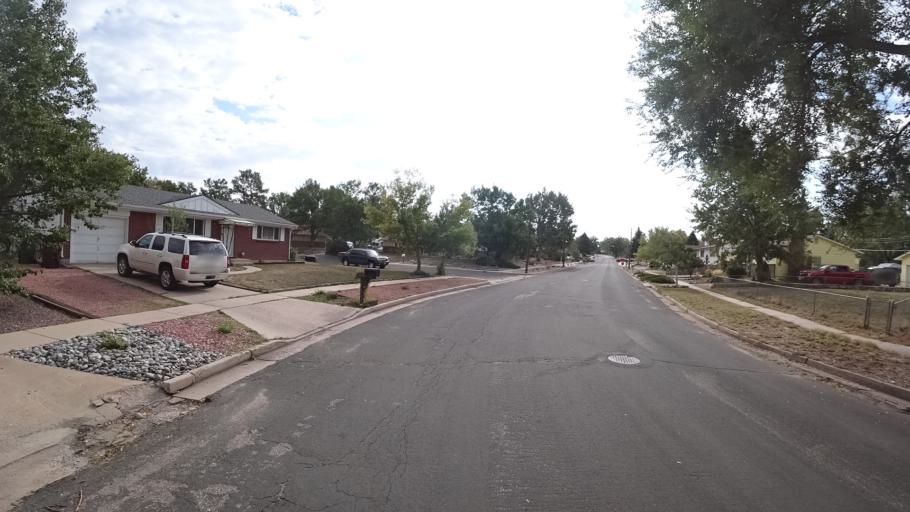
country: US
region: Colorado
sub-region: El Paso County
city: Cimarron Hills
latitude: 38.8456
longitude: -104.7537
